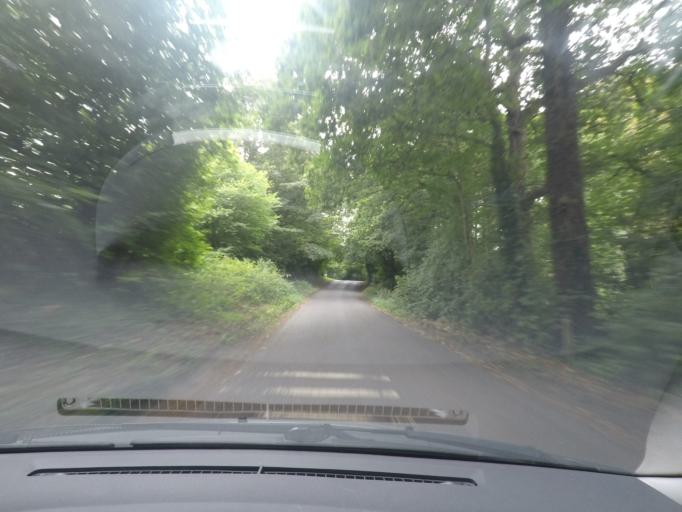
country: GB
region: England
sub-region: Wiltshire
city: Huish
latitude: 51.3492
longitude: -1.7901
